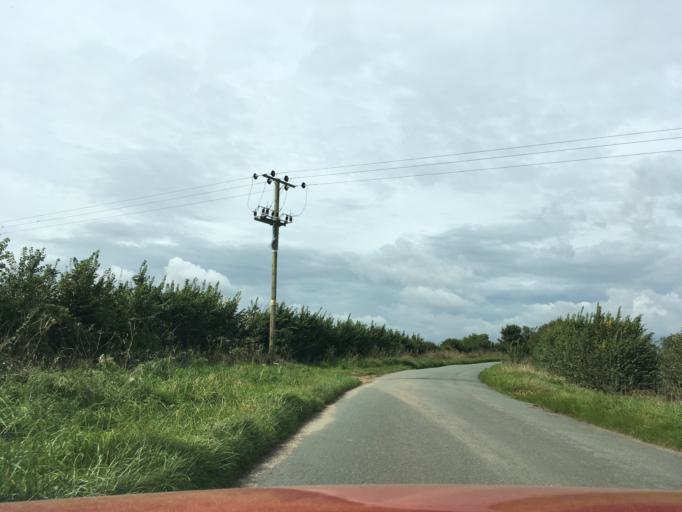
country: GB
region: England
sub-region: South Gloucestershire
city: Thornbury
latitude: 51.6176
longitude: -2.5608
